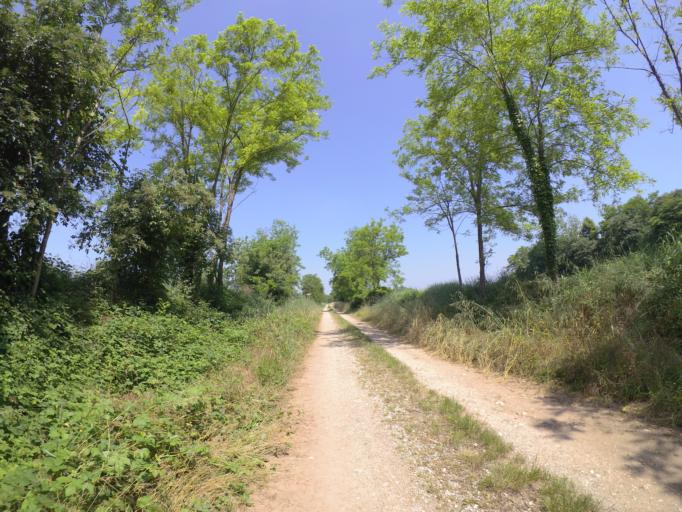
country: IT
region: Friuli Venezia Giulia
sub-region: Provincia di Udine
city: Bertiolo
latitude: 45.9657
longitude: 13.0844
